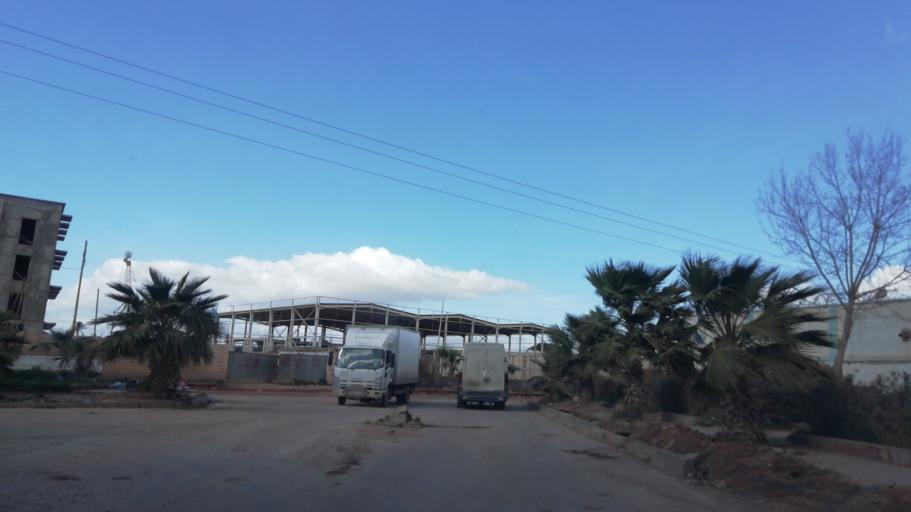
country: DZ
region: Oran
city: Es Senia
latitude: 35.6243
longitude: -0.5838
